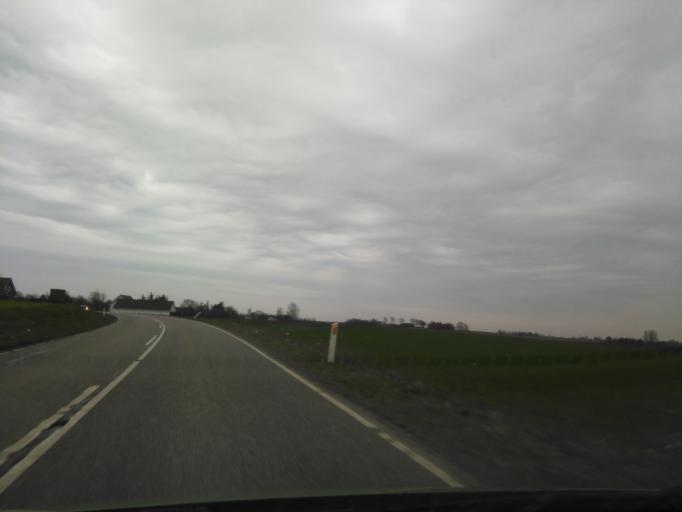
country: DK
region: Central Jutland
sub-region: Randers Kommune
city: Spentrup
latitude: 56.5818
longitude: 9.9939
